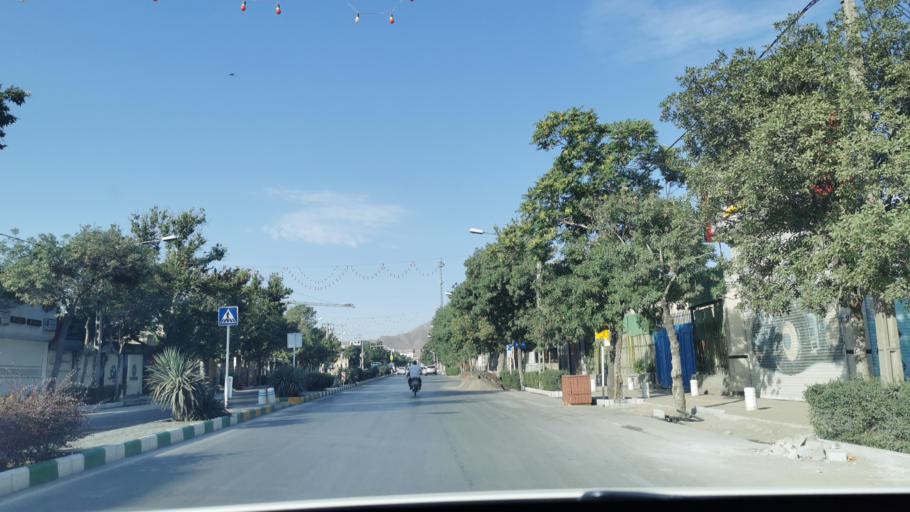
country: IR
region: Razavi Khorasan
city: Mashhad
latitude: 36.2692
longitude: 59.6103
